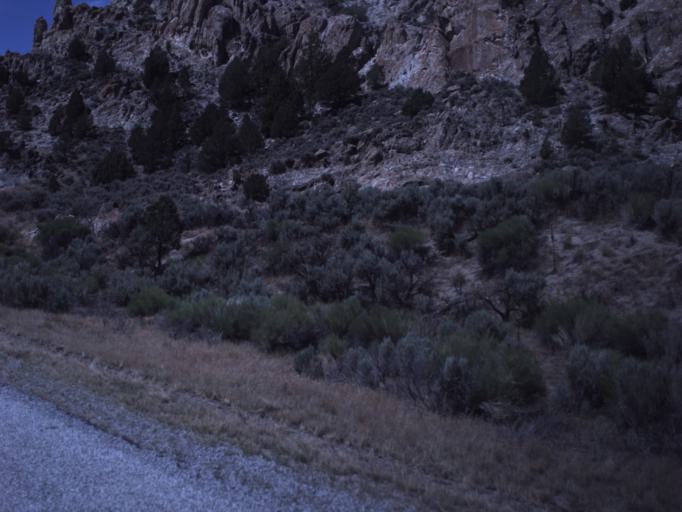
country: US
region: Utah
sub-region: Garfield County
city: Panguitch
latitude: 38.0371
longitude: -112.3558
